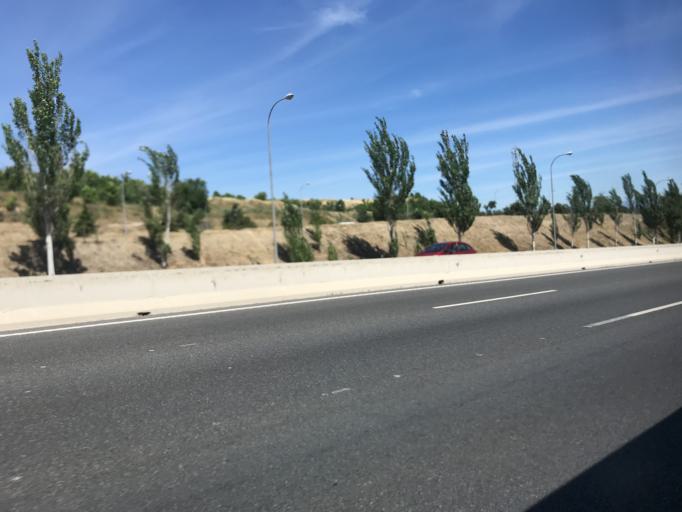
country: ES
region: Madrid
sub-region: Provincia de Madrid
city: San Blas
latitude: 40.4372
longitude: -3.5935
